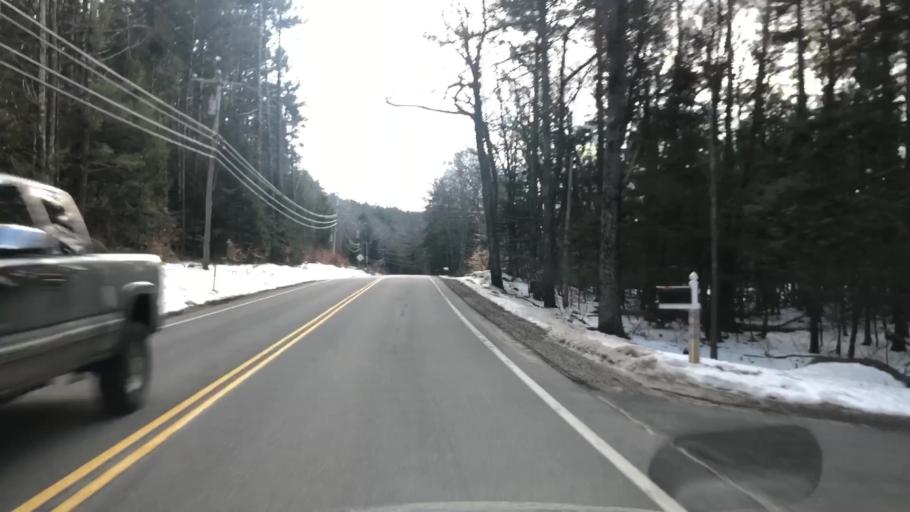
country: US
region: New Hampshire
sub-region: Hillsborough County
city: Mont Vernon
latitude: 42.8755
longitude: -71.6690
